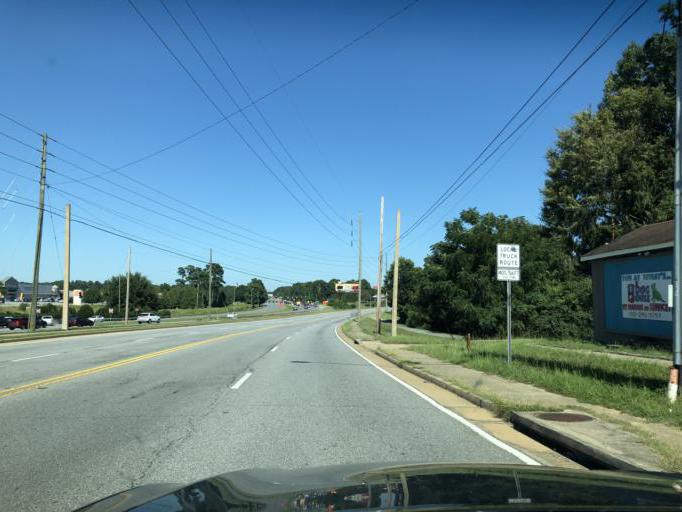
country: US
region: Georgia
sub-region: Muscogee County
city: Columbus
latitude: 32.5053
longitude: -84.9458
